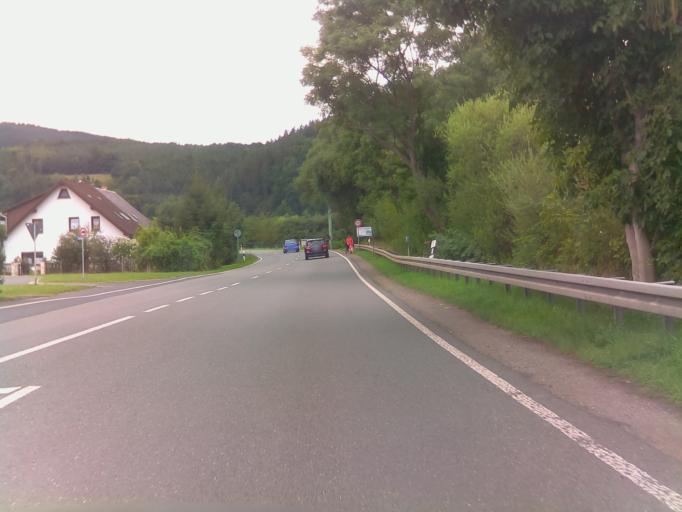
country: DE
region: Thuringia
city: Kaulsdorf
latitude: 50.6227
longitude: 11.4285
